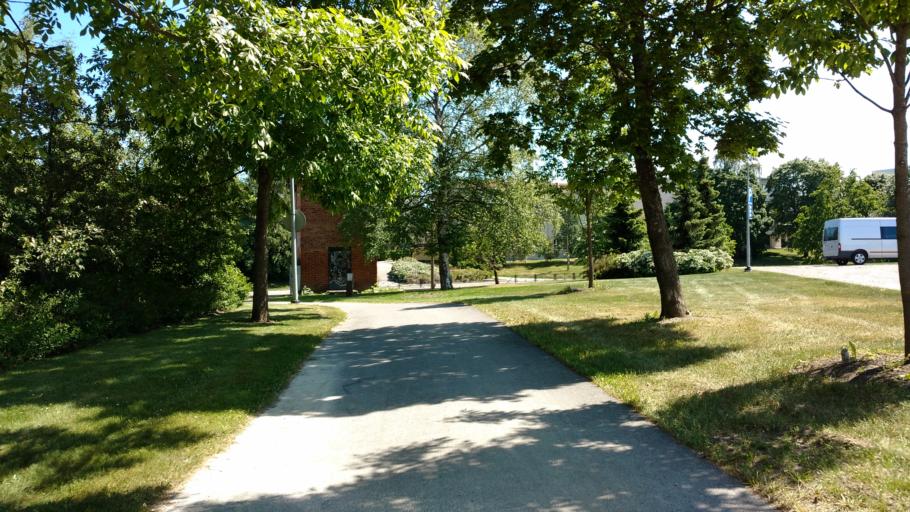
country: FI
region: Varsinais-Suomi
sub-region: Salo
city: Salo
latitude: 60.3891
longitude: 23.1281
